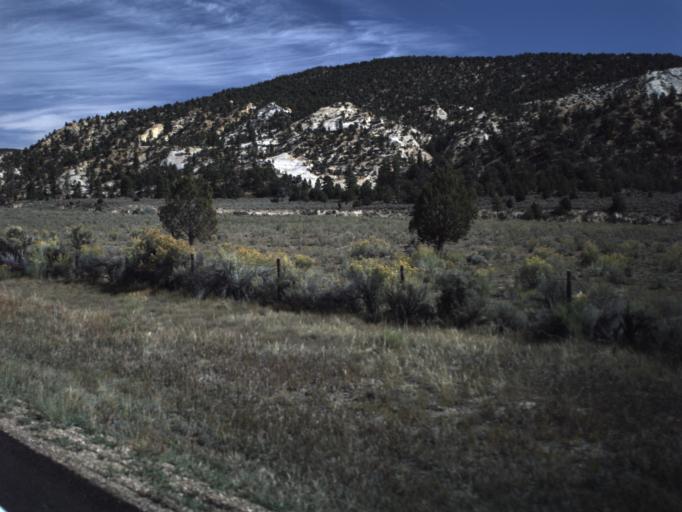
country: US
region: Utah
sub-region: Garfield County
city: Panguitch
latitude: 37.7043
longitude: -111.7898
